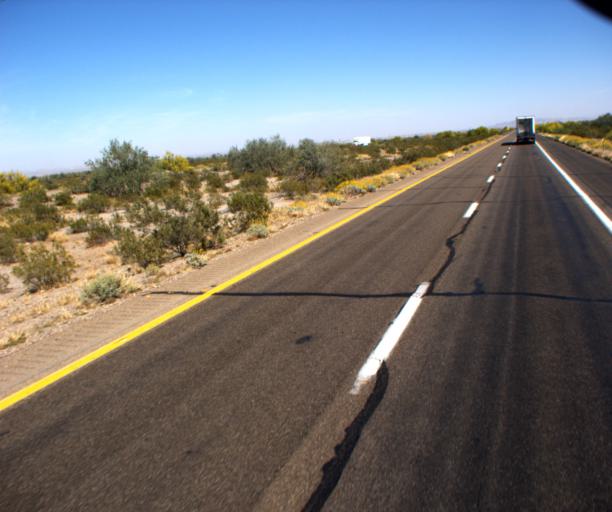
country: US
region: Arizona
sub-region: Pinal County
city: Maricopa
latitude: 32.8298
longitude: -112.0190
